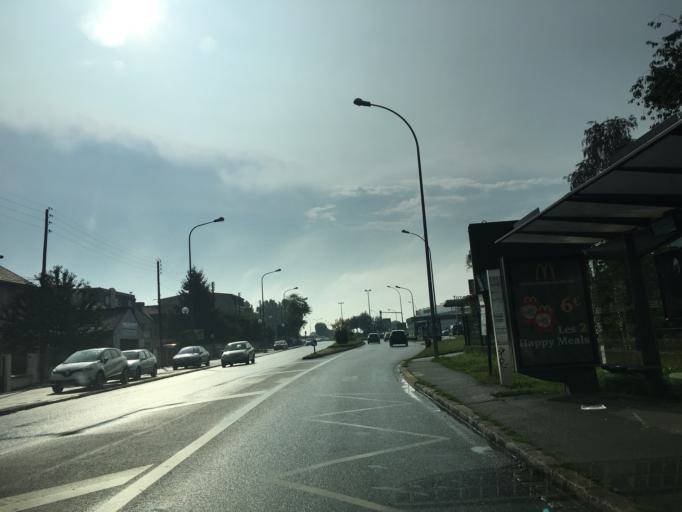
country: FR
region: Ile-de-France
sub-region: Departement du Val-de-Marne
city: Chennevieres-sur-Marne
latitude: 48.8005
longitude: 2.5424
